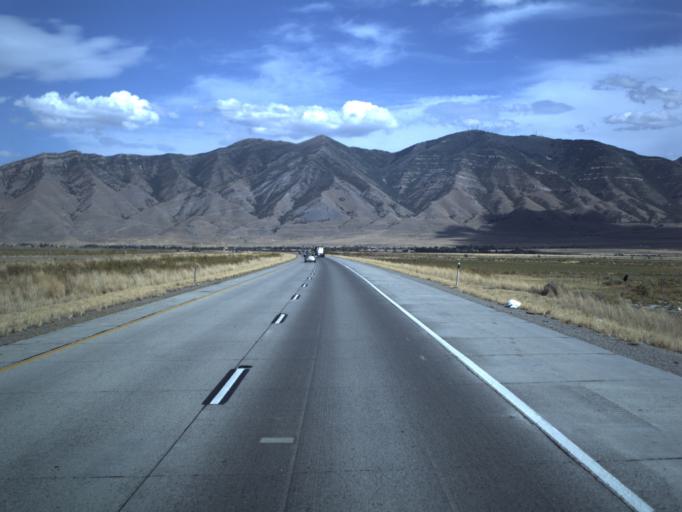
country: US
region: Utah
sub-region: Tooele County
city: Stansbury park
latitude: 40.6626
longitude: -112.3290
